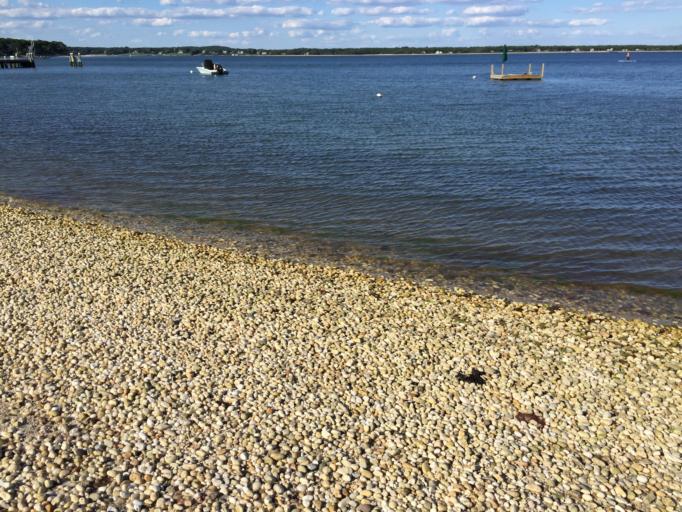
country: US
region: New York
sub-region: Suffolk County
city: Southold
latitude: 41.0373
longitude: -72.3893
